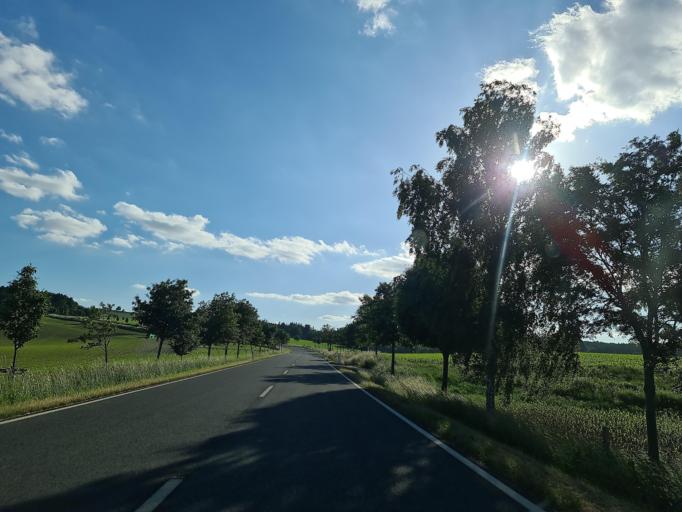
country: DE
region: Saxony
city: Reuth
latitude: 50.4787
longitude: 11.9825
